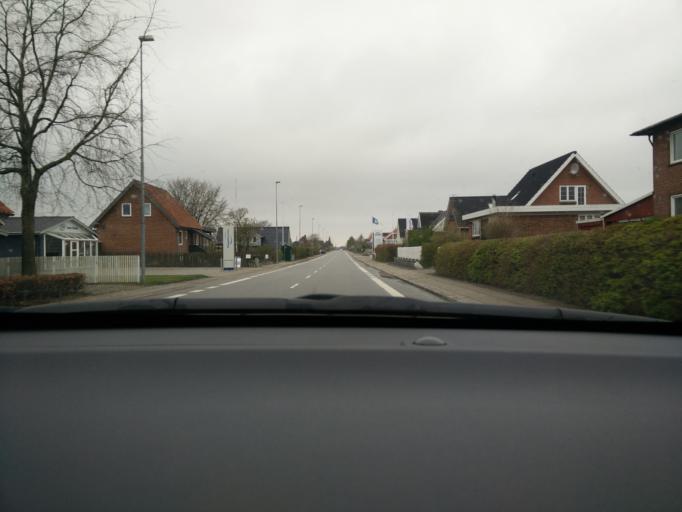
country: DK
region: Central Jutland
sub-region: Skive Kommune
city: Hojslev
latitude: 56.5447
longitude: 9.1262
